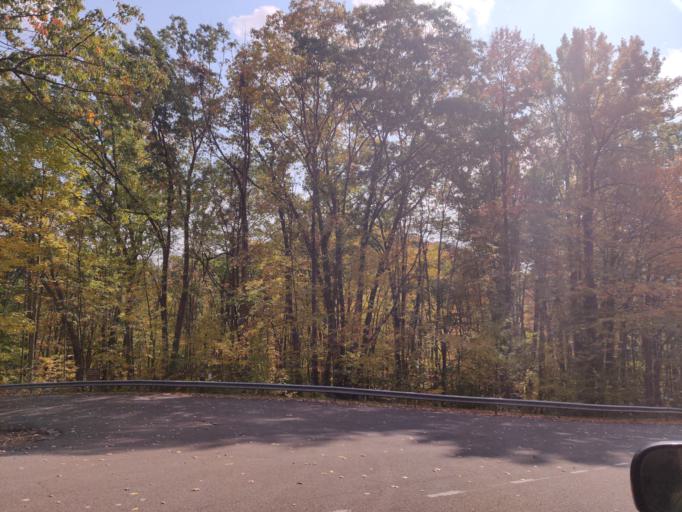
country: US
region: Pennsylvania
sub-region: Warren County
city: Sheffield
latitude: 41.8282
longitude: -78.9667
